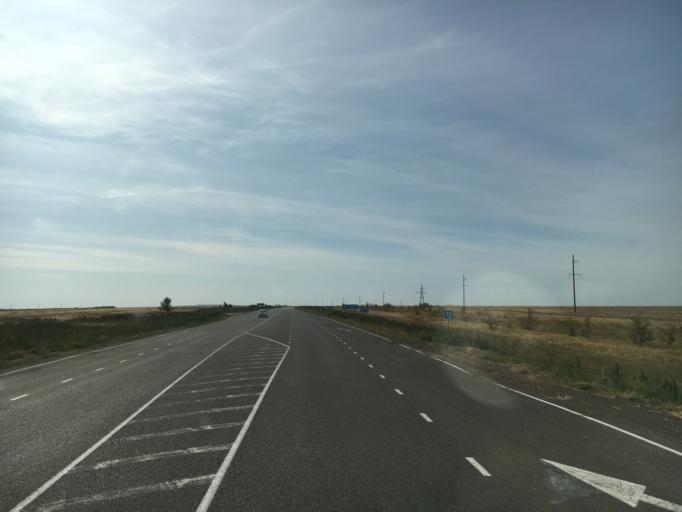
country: KZ
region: Batys Qazaqstan
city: Peremetnoe
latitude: 51.1203
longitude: 50.7408
